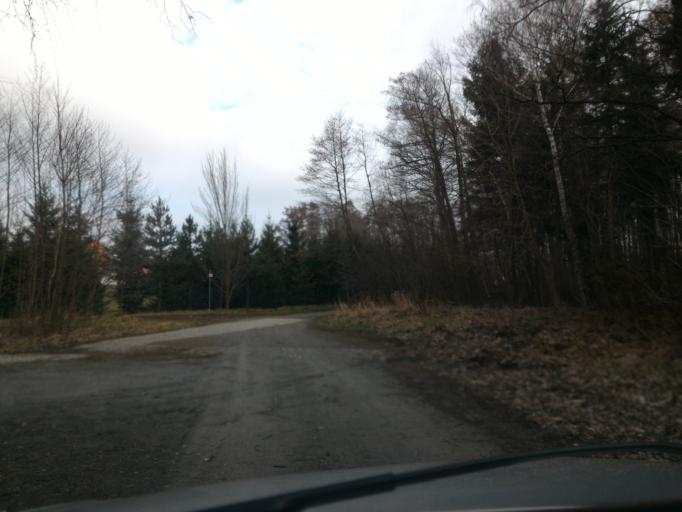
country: DE
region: Saxony
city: Olbersdorf
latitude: 50.8621
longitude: 14.7613
